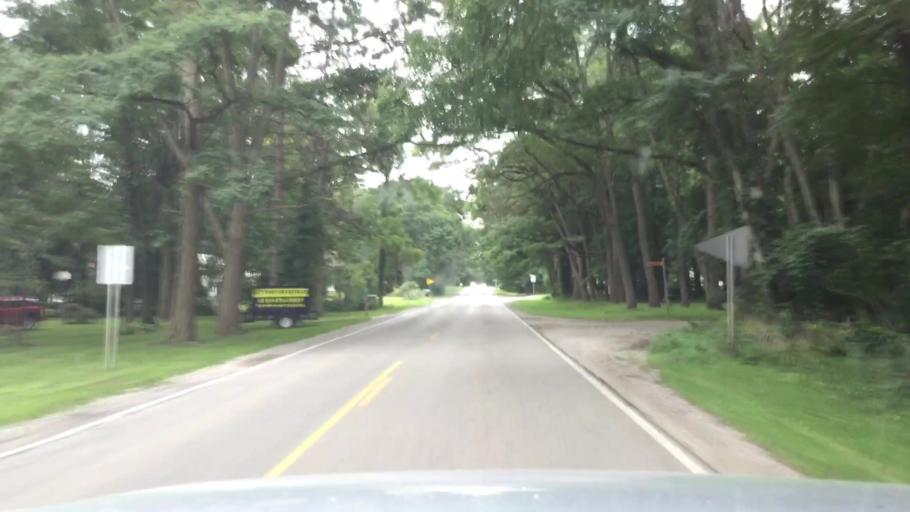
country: US
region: Michigan
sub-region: Genesee County
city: Argentine
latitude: 42.8103
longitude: -83.8899
